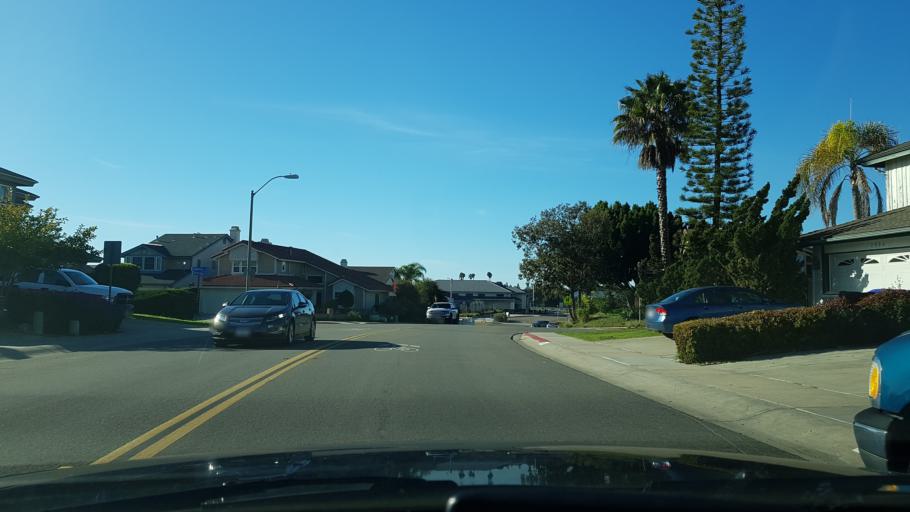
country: US
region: California
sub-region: San Diego County
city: Fairbanks Ranch
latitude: 32.9054
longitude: -117.1536
